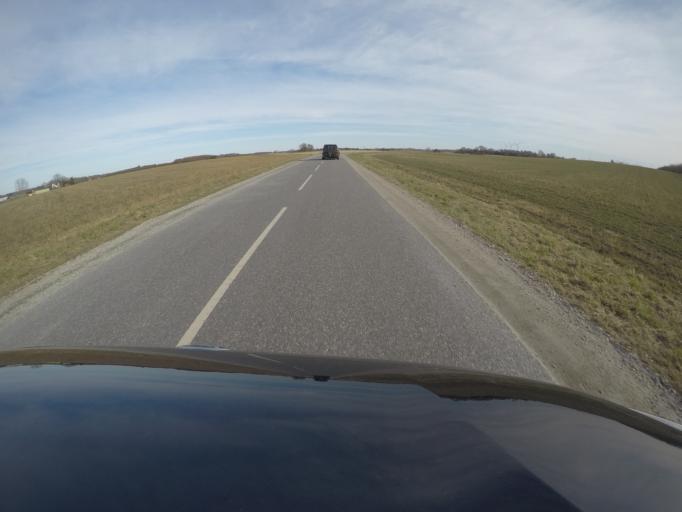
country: DK
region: Capital Region
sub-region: Halsnaes Kommune
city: Liseleje
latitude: 55.9830
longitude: 11.9483
